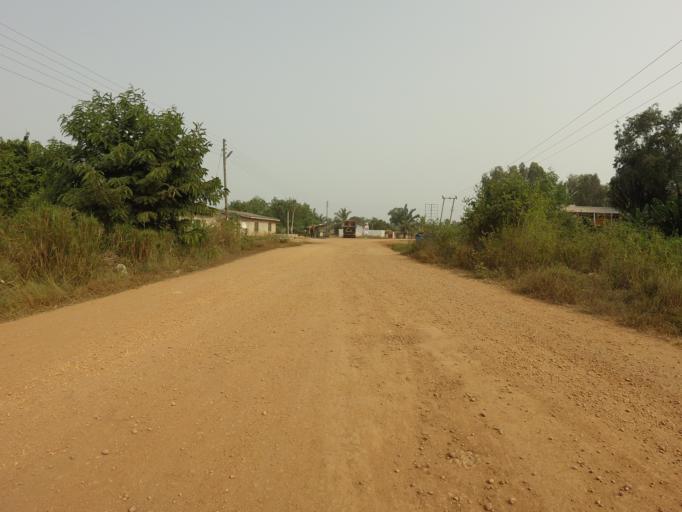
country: GH
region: Volta
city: Anloga
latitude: 5.9899
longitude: 0.5964
